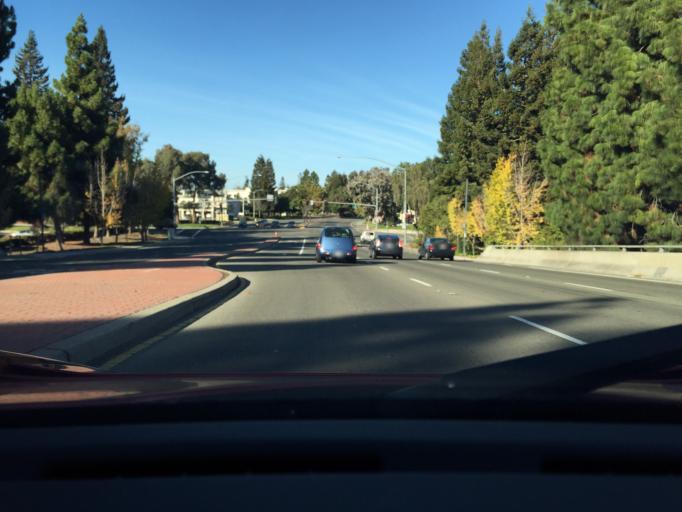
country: US
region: California
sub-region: Santa Clara County
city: Sunnyvale
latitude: 37.3741
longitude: -122.0138
